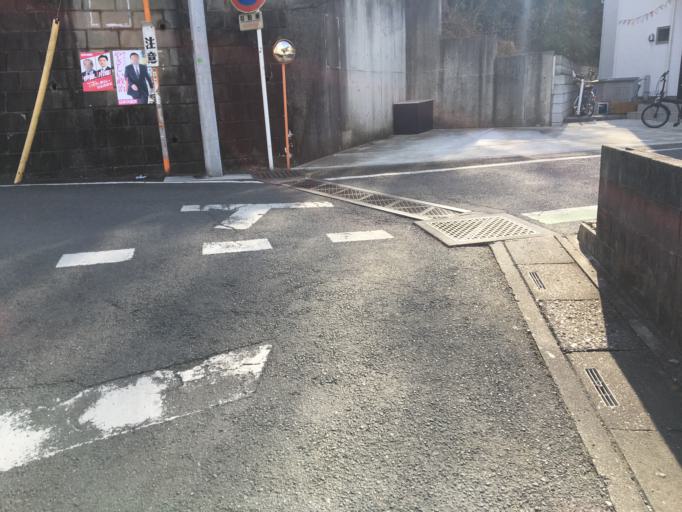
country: JP
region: Saitama
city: Oi
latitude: 35.8456
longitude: 139.5497
